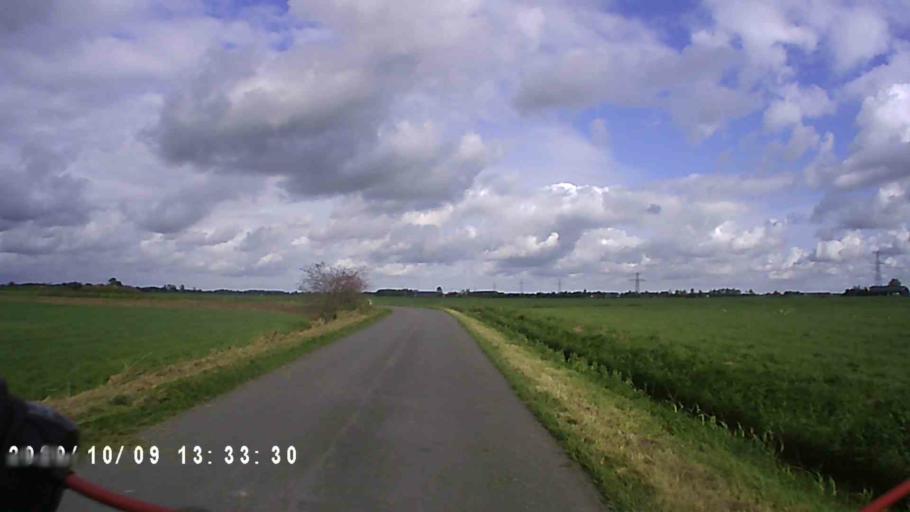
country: NL
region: Groningen
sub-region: Gemeente Zuidhorn
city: Aduard
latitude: 53.2895
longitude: 6.4726
